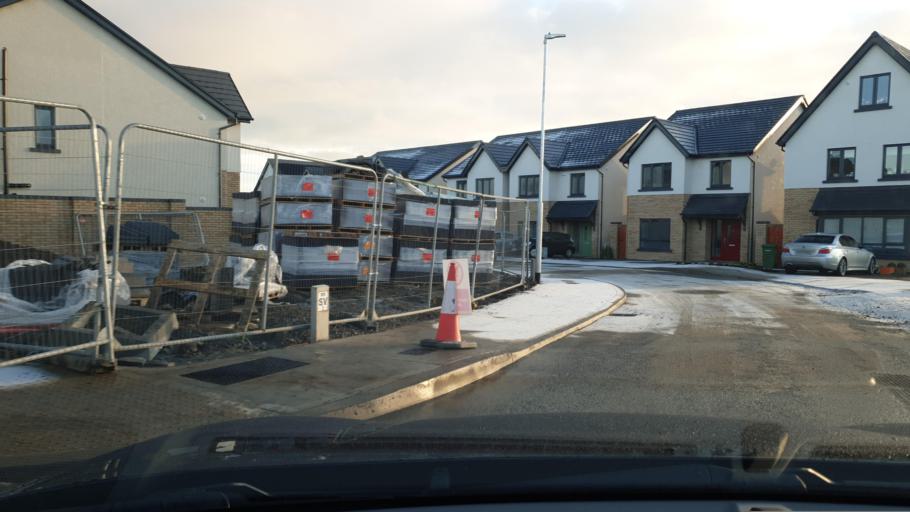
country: IE
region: Leinster
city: Lusk
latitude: 53.5320
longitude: -6.1576
